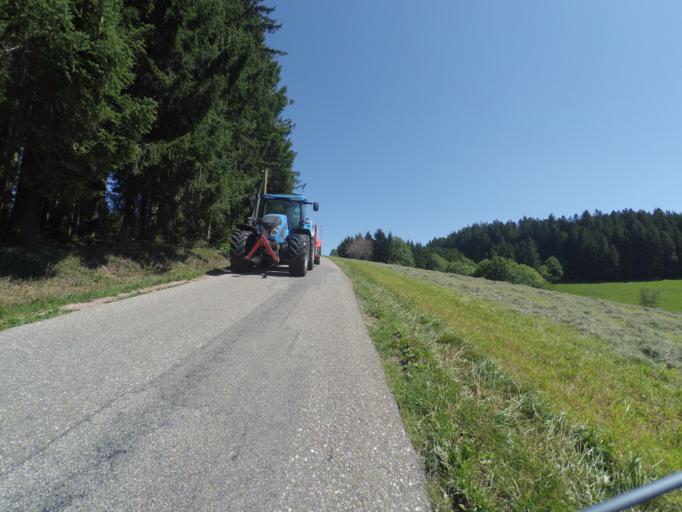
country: DE
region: Baden-Wuerttemberg
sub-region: Freiburg Region
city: Gutenbach
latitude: 48.0615
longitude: 8.1539
